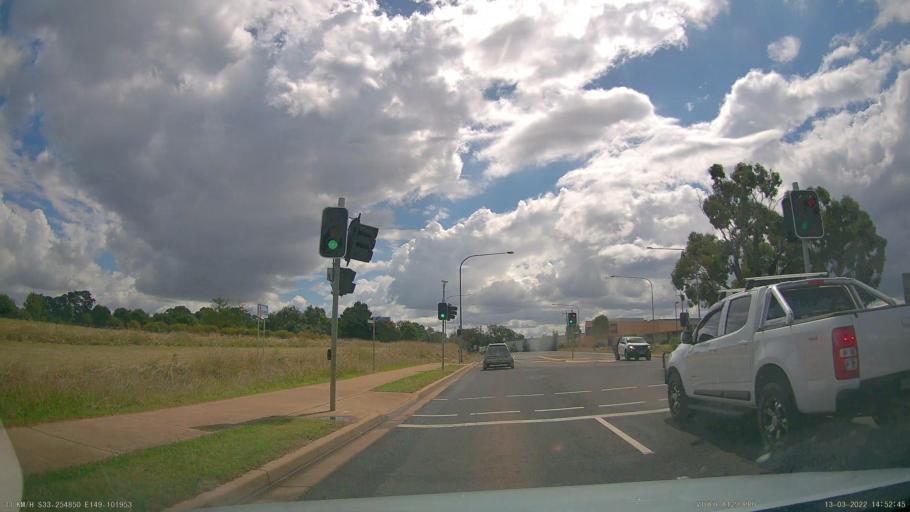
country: AU
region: New South Wales
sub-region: Orange Municipality
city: Orange
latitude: -33.2548
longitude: 149.1019
